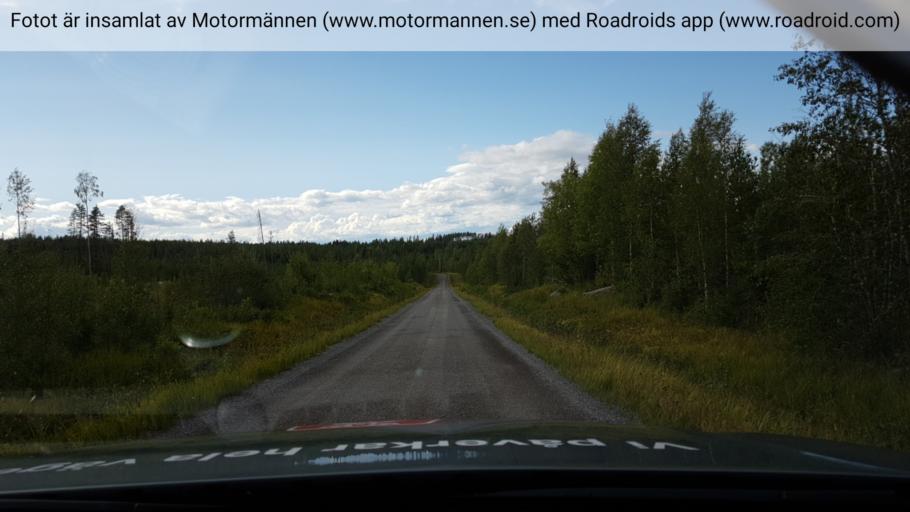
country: SE
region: Jaemtland
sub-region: OEstersunds Kommun
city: Lit
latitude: 63.2988
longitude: 15.3218
